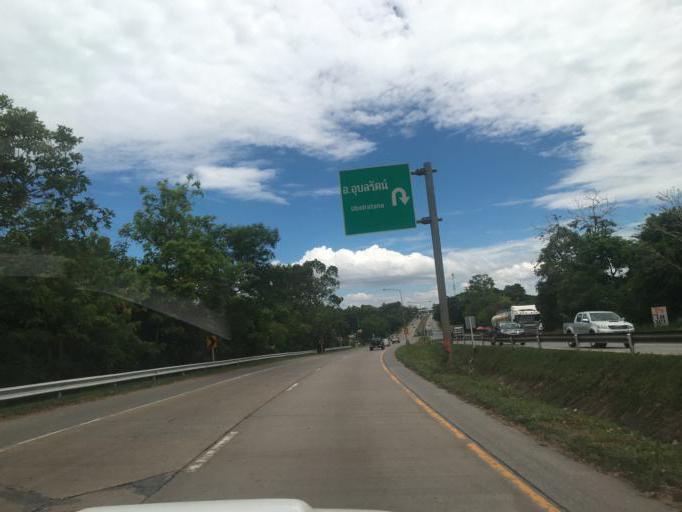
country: TH
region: Khon Kaen
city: Nam Phong
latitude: 16.6672
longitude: 102.8042
